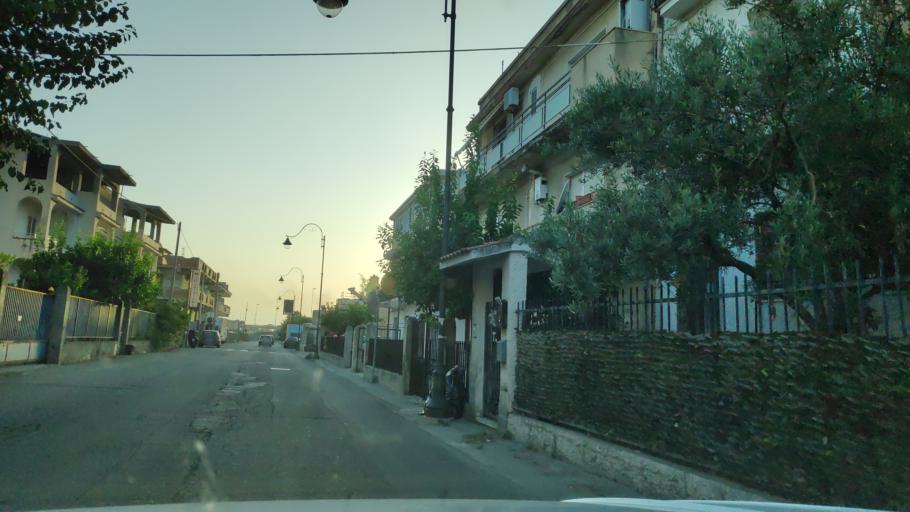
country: IT
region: Calabria
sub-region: Provincia di Reggio Calabria
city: Bova Marina
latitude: 37.9291
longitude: 15.9070
